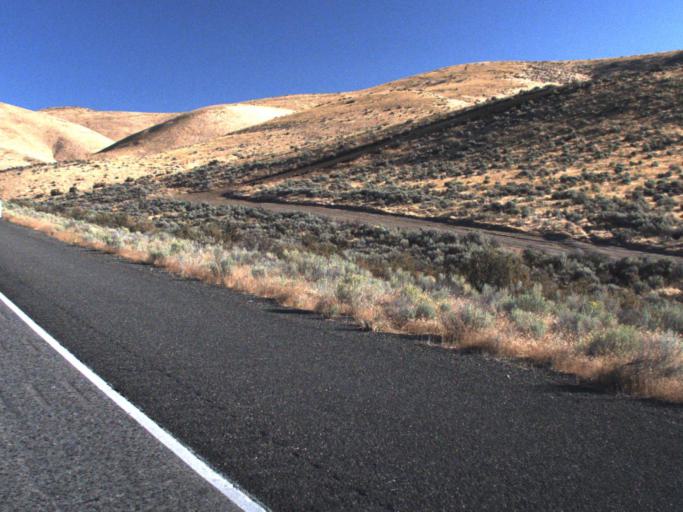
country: US
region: Washington
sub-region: Kittitas County
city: Kittitas
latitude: 46.8535
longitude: -120.3921
